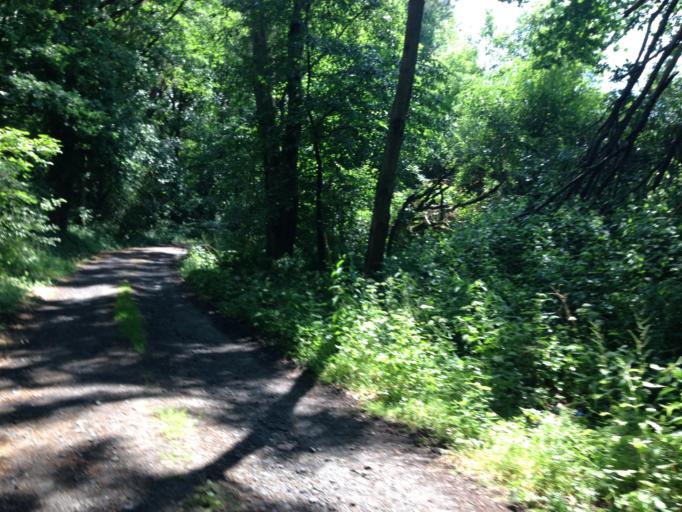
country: DE
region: Hesse
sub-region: Regierungsbezirk Giessen
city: Marburg an der Lahn
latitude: 50.8504
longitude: 8.7523
